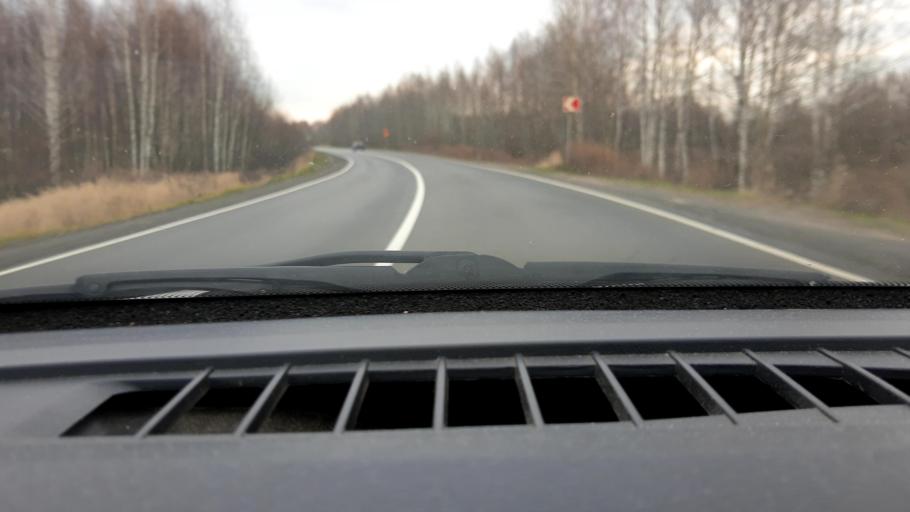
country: RU
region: Nizjnij Novgorod
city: Neklyudovo
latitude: 56.5281
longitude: 43.8248
